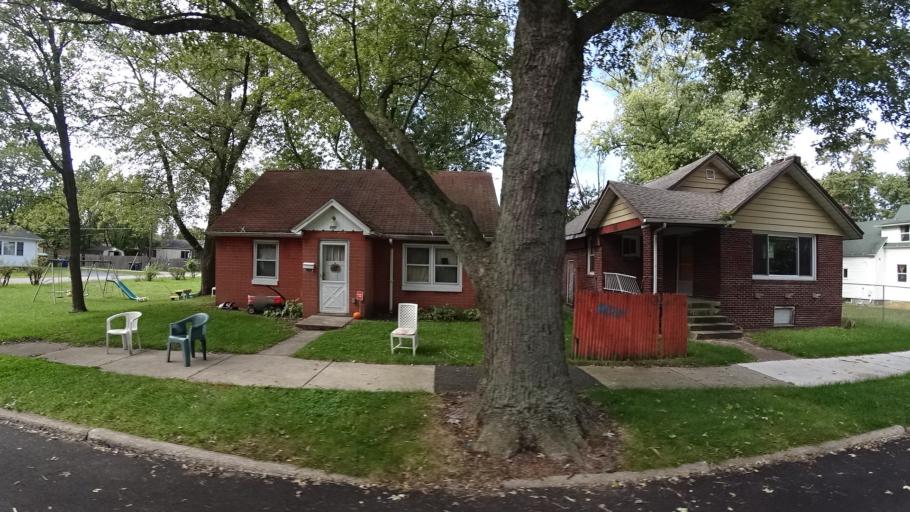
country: US
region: Indiana
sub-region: LaPorte County
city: Trail Creek
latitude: 41.7122
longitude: -86.8728
